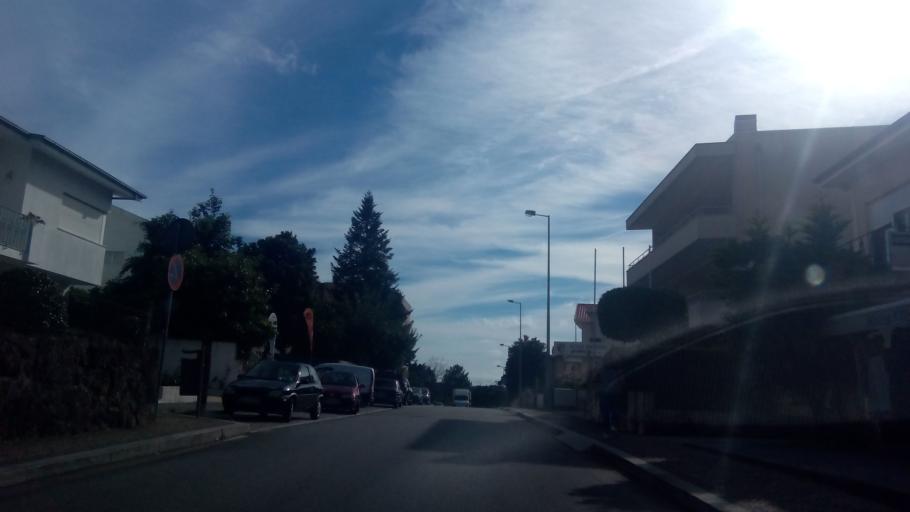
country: PT
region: Porto
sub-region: Paredes
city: Paredes
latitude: 41.2064
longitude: -8.3316
